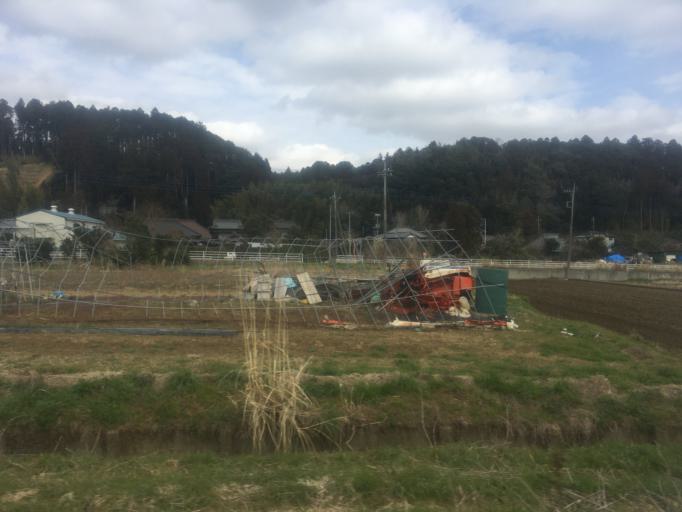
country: JP
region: Chiba
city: Naruto
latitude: 35.6124
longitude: 140.3840
